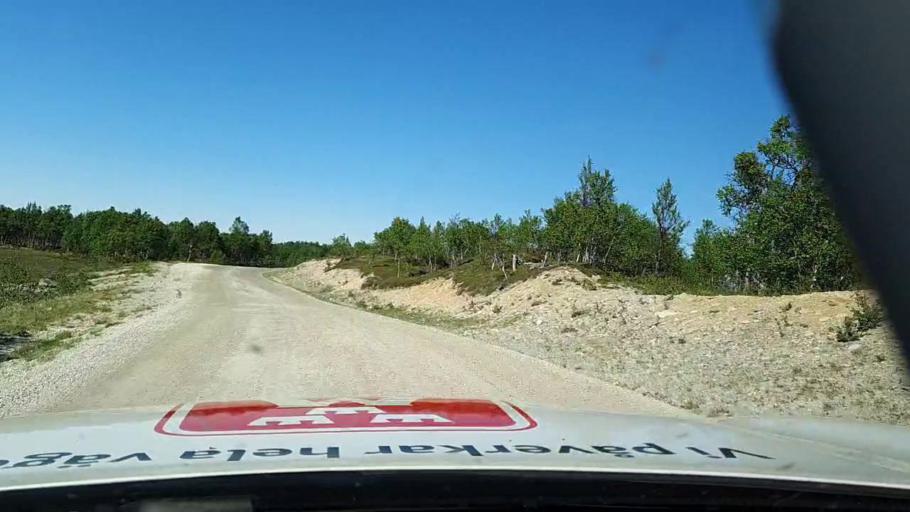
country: SE
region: Jaemtland
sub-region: Are Kommun
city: Are
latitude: 62.6318
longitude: 12.6462
